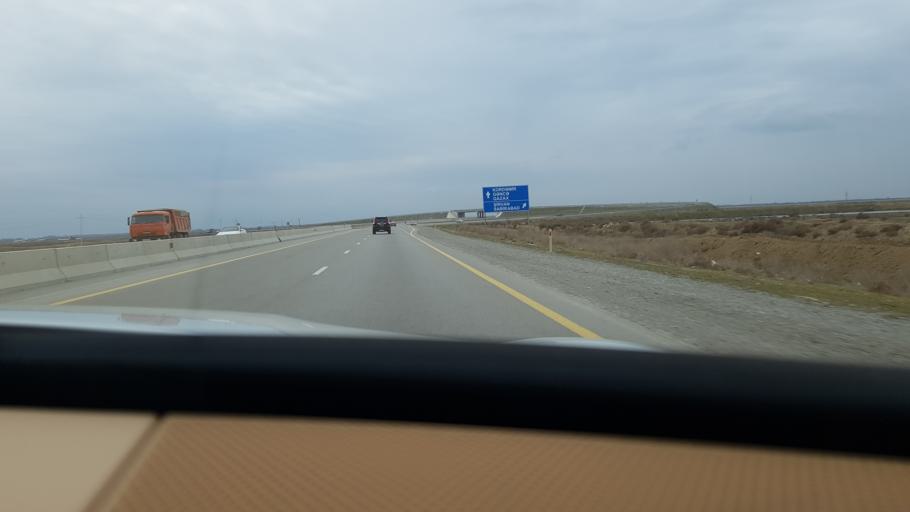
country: AZ
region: Haciqabul
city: Haciqabul
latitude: 40.0092
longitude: 48.9135
